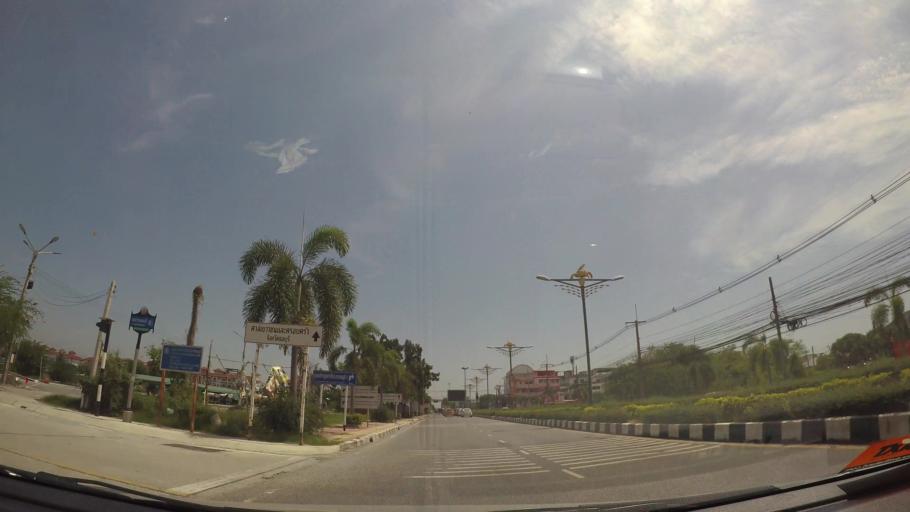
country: TH
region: Chon Buri
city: Chon Buri
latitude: 13.3362
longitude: 100.9510
